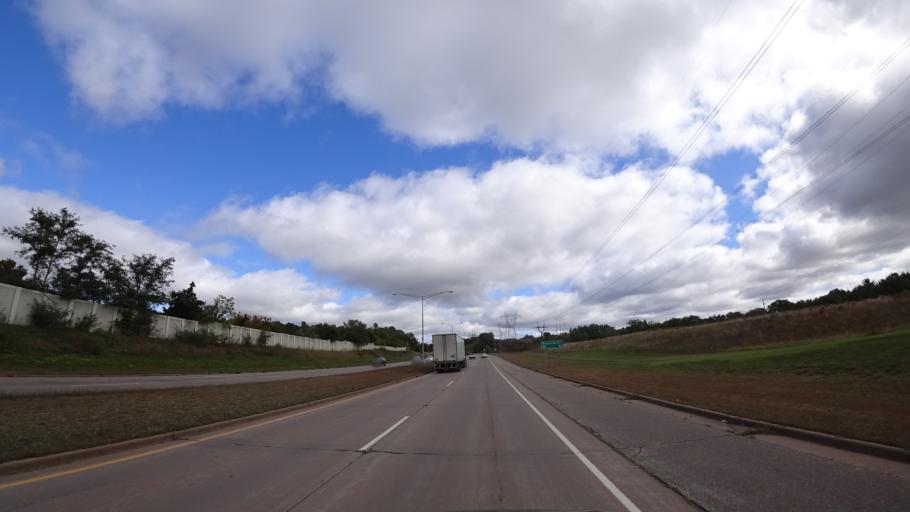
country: US
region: Wisconsin
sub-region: Eau Claire County
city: Eau Claire
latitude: 44.8408
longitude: -91.4909
